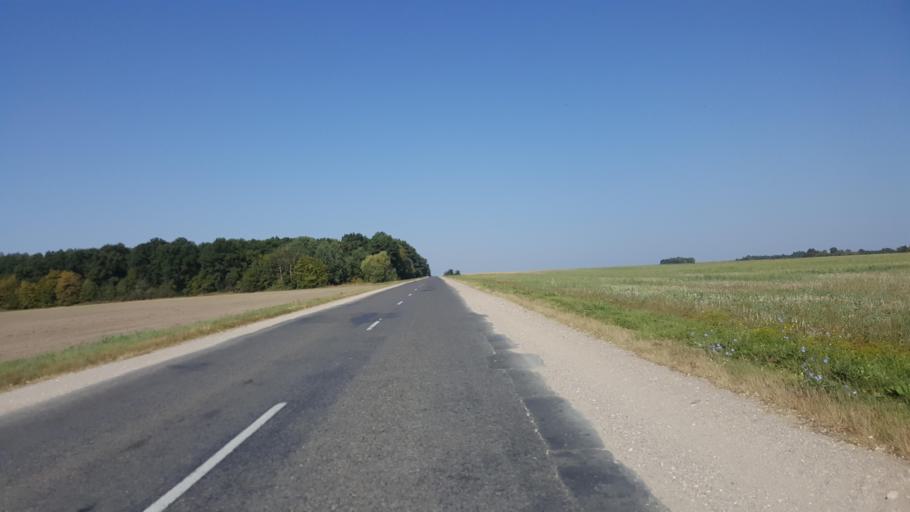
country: BY
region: Brest
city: Kamyanyets
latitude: 52.4136
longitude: 23.7131
